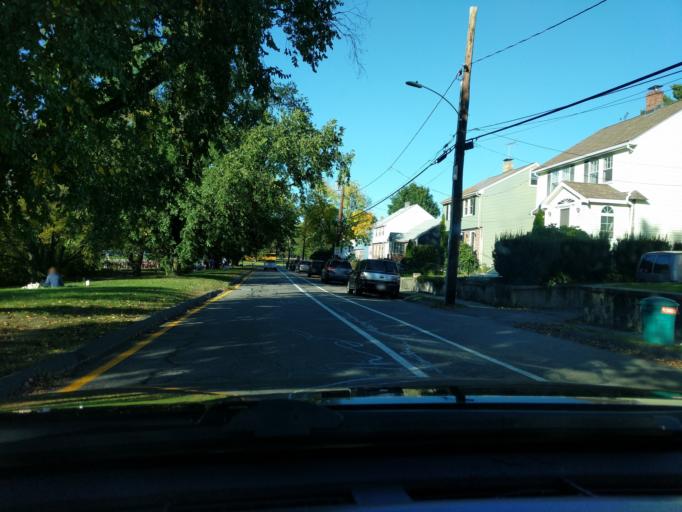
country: US
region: Massachusetts
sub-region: Middlesex County
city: Belmont
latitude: 42.3933
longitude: -71.1621
